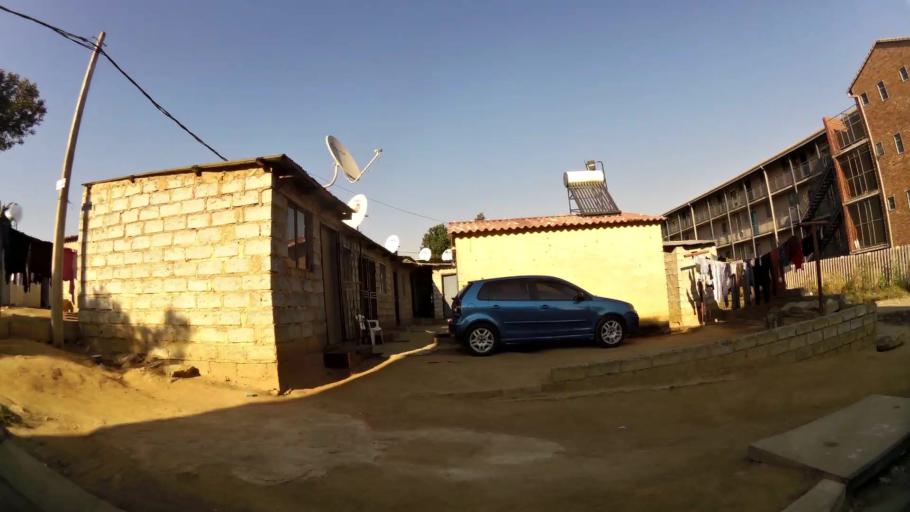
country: ZA
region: Gauteng
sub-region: City of Johannesburg Metropolitan Municipality
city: Modderfontein
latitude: -26.0963
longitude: 28.1119
